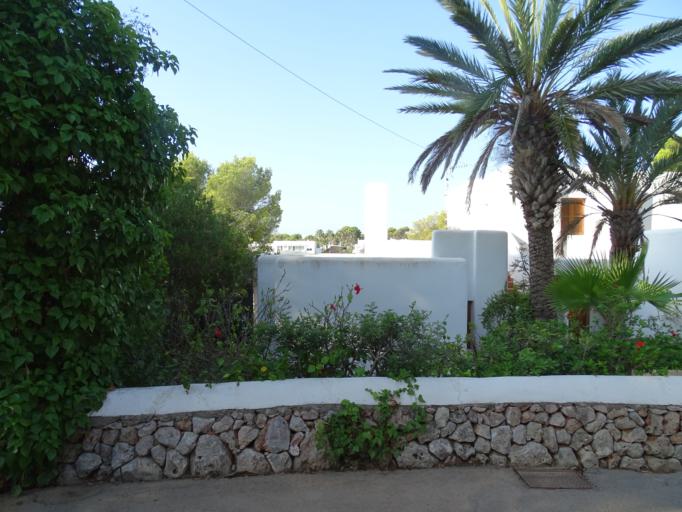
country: ES
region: Balearic Islands
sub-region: Illes Balears
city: Santanyi
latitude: 39.3685
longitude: 3.2290
